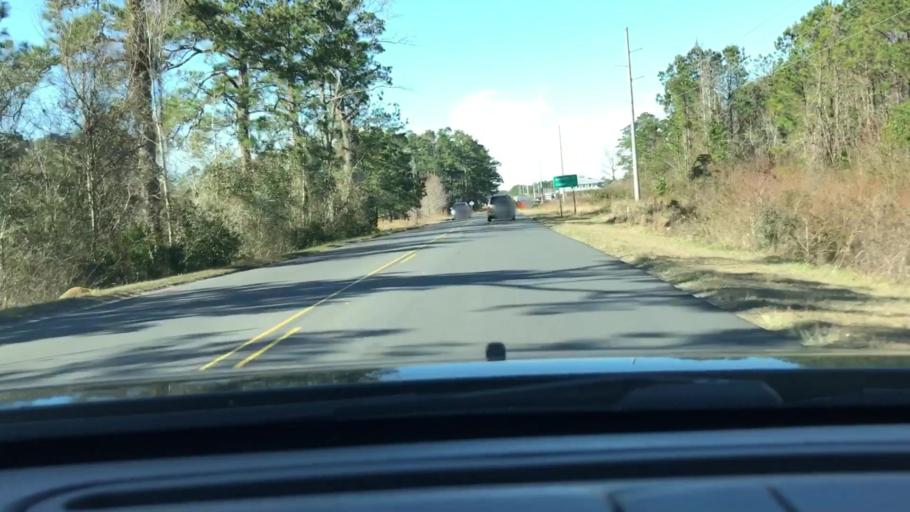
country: US
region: North Carolina
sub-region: Brunswick County
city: Shallotte
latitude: 33.9699
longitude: -78.3948
